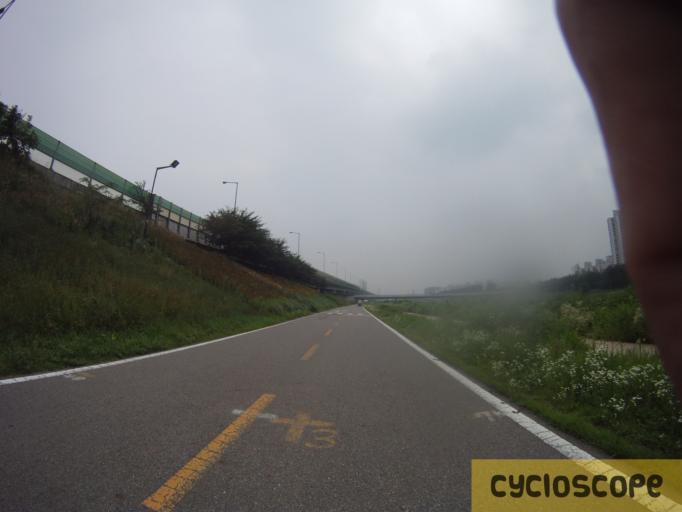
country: KR
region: Gyeonggi-do
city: Kwangmyong
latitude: 37.4580
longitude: 126.8918
